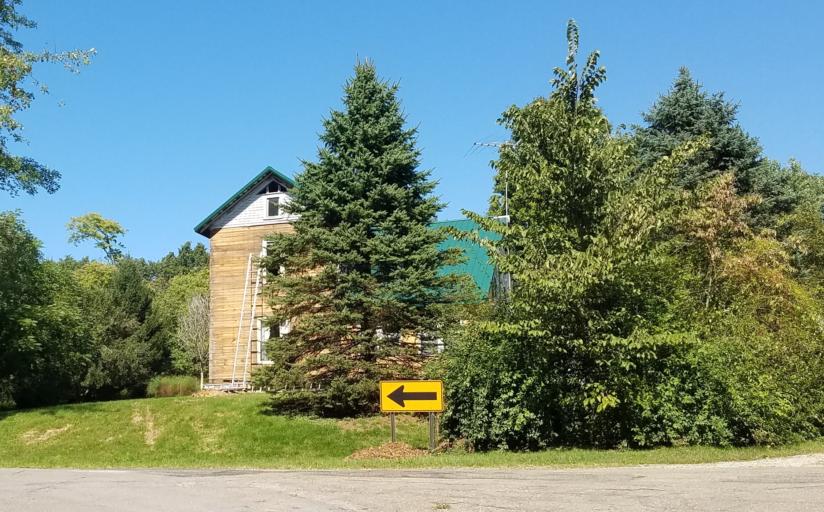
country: US
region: Ohio
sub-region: Ashland County
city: Loudonville
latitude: 40.5649
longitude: -82.3511
